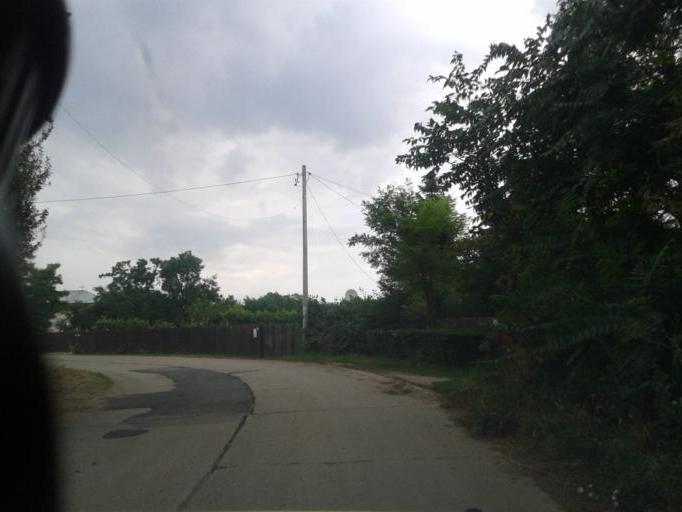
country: RO
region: Ialomita
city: Sinesti
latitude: 44.5459
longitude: 26.4346
